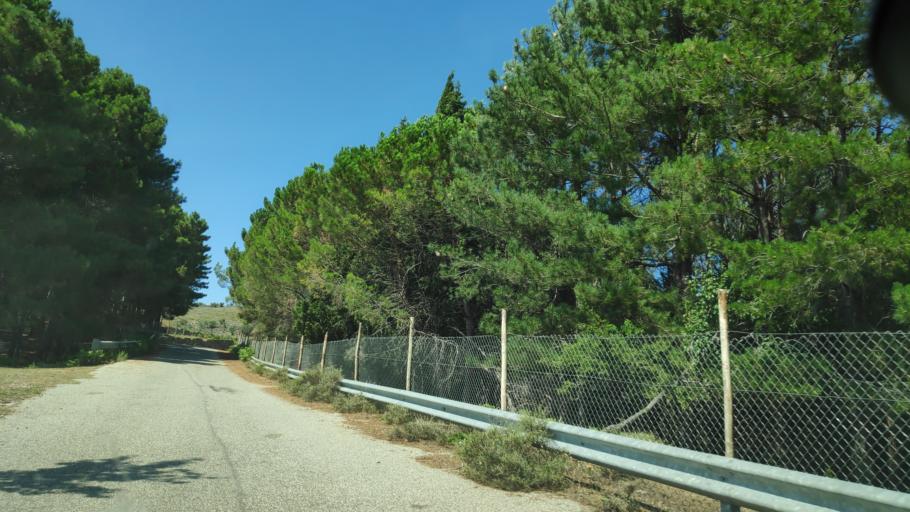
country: IT
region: Calabria
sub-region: Provincia di Reggio Calabria
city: Bova
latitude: 38.0151
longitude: 15.9349
